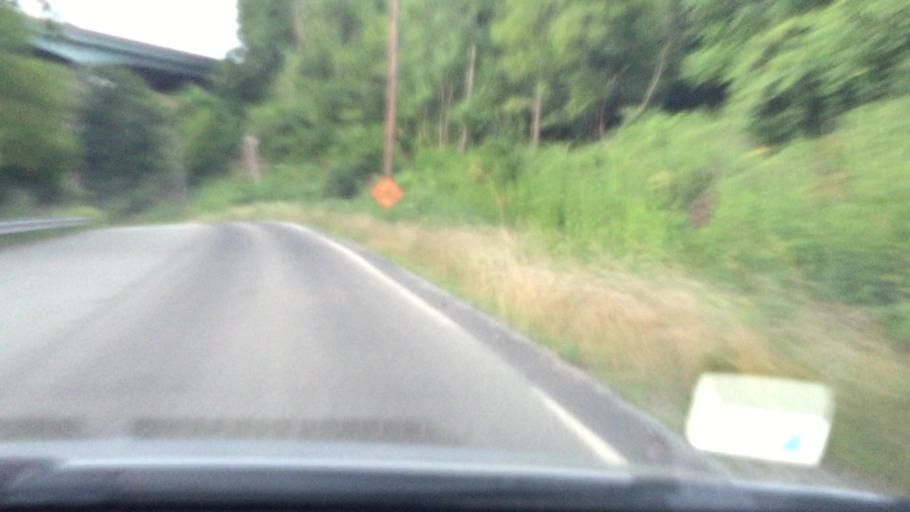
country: US
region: Pennsylvania
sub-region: Allegheny County
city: Monroeville
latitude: 40.4410
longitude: -79.7988
